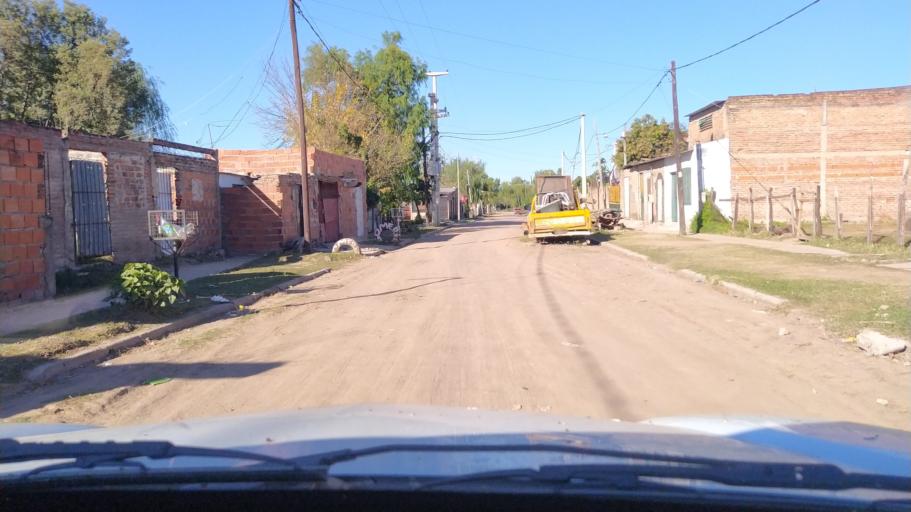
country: AR
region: Corrientes
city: Corrientes
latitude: -27.4960
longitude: -58.8093
